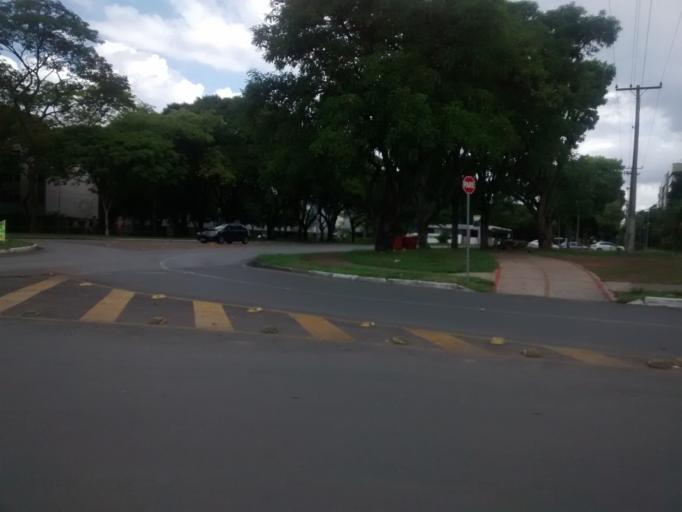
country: BR
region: Federal District
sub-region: Brasilia
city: Brasilia
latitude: -15.7572
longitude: -47.8823
